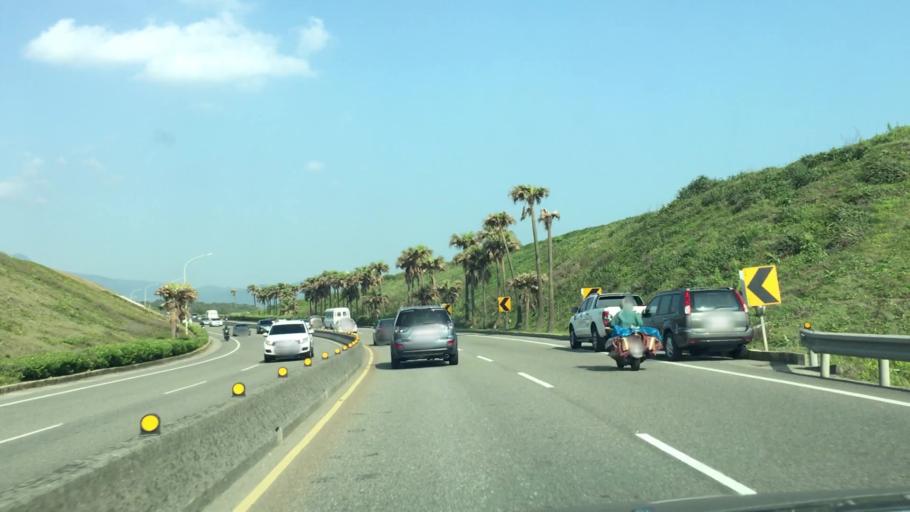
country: TW
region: Taiwan
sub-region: Keelung
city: Keelung
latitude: 25.2048
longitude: 121.6664
